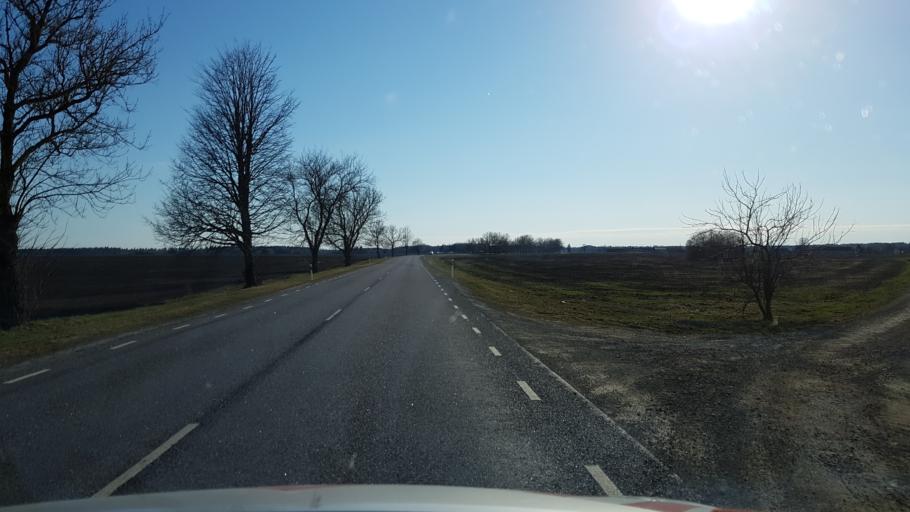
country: EE
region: Ida-Virumaa
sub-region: Johvi vald
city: Johvi
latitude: 59.3410
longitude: 27.3541
